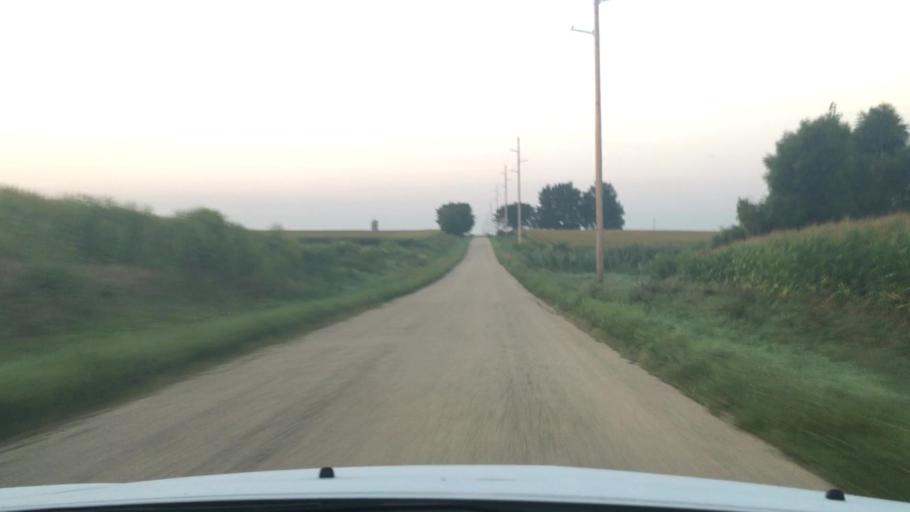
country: US
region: Illinois
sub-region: Ogle County
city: Rochelle
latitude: 41.8656
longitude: -89.0007
